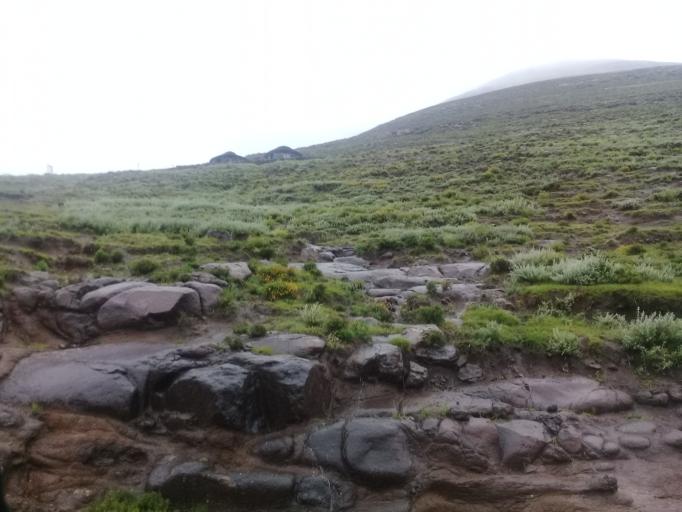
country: LS
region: Mokhotlong
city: Mokhotlong
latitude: -29.3896
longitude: 28.9616
